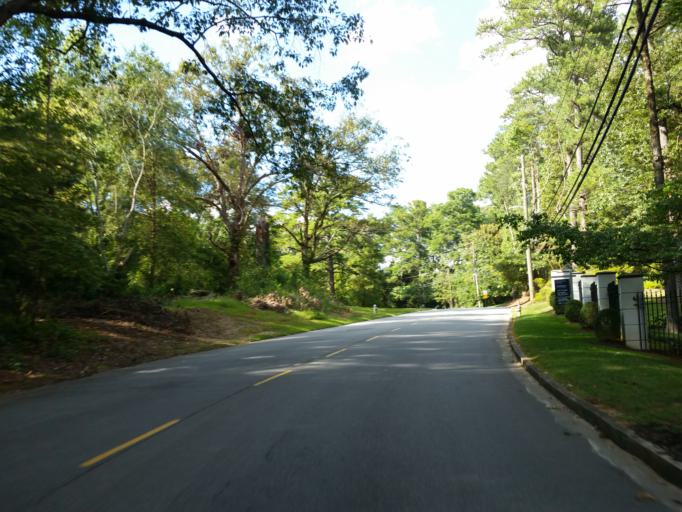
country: US
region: Georgia
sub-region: Cobb County
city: Vinings
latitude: 33.8735
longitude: -84.4097
